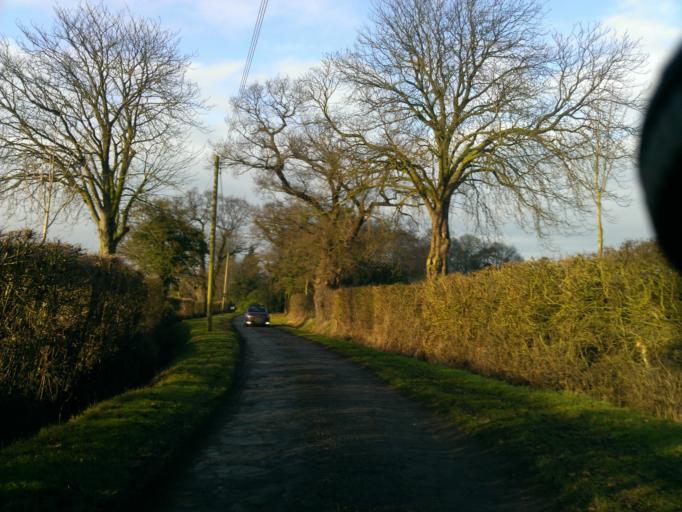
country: GB
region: England
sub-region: Suffolk
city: Sudbury
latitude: 52.0374
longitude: 0.6885
